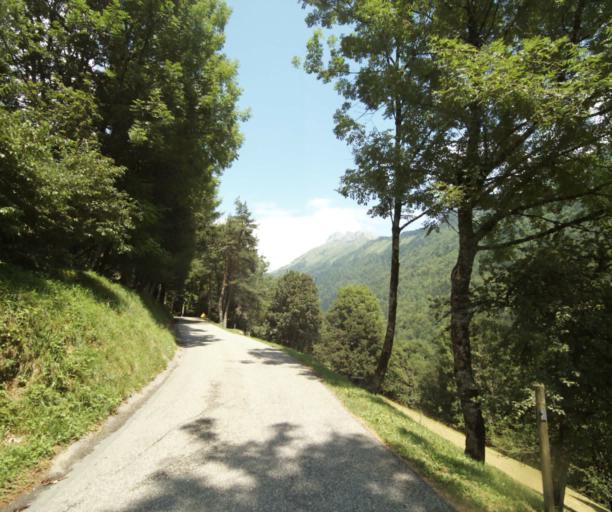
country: FR
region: Rhone-Alpes
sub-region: Departement de la Haute-Savoie
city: Thones
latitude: 45.9058
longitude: 6.3100
